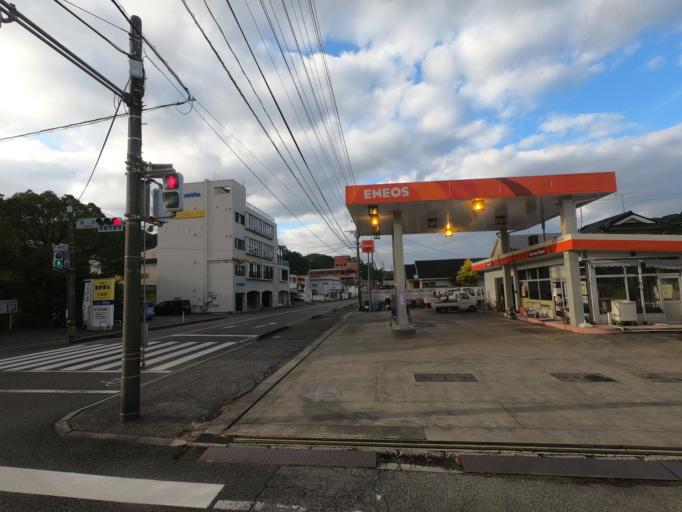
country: JP
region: Kumamoto
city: Minamata
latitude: 32.2724
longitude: 130.5015
